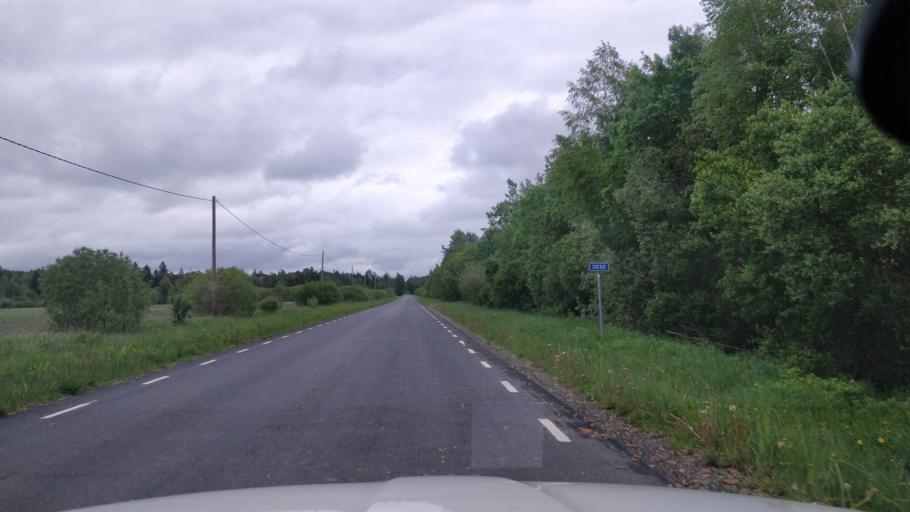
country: EE
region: Raplamaa
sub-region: Maerjamaa vald
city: Marjamaa
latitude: 58.7578
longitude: 24.2442
